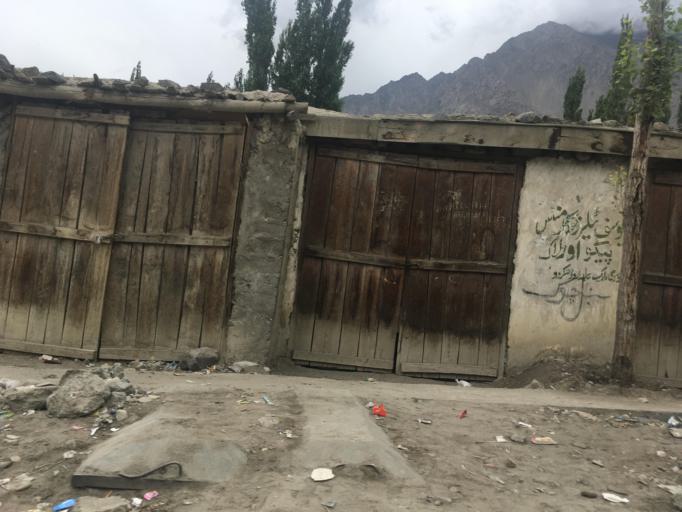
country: PK
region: Gilgit-Baltistan
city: Skardu
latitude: 35.2861
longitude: 75.6456
